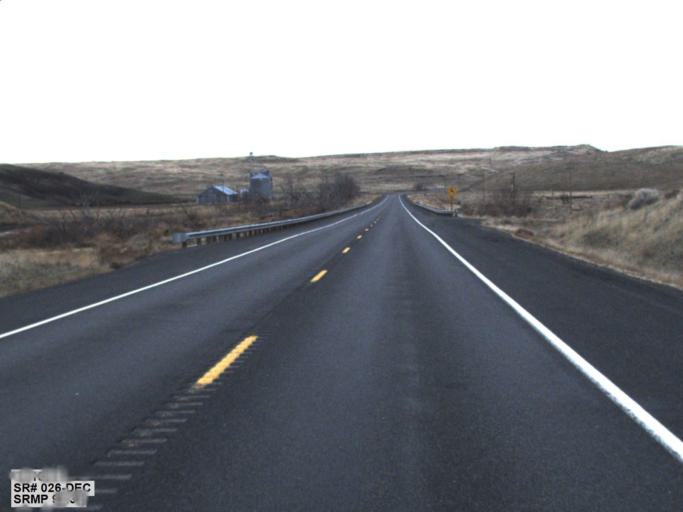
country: US
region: Washington
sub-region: Columbia County
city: Dayton
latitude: 46.7652
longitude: -118.0152
